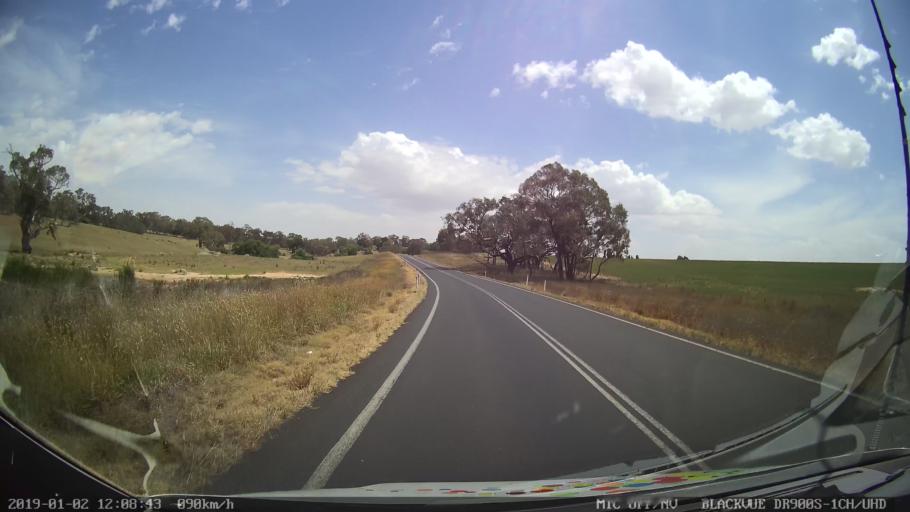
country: AU
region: New South Wales
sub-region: Young
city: Young
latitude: -34.4806
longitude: 148.2744
